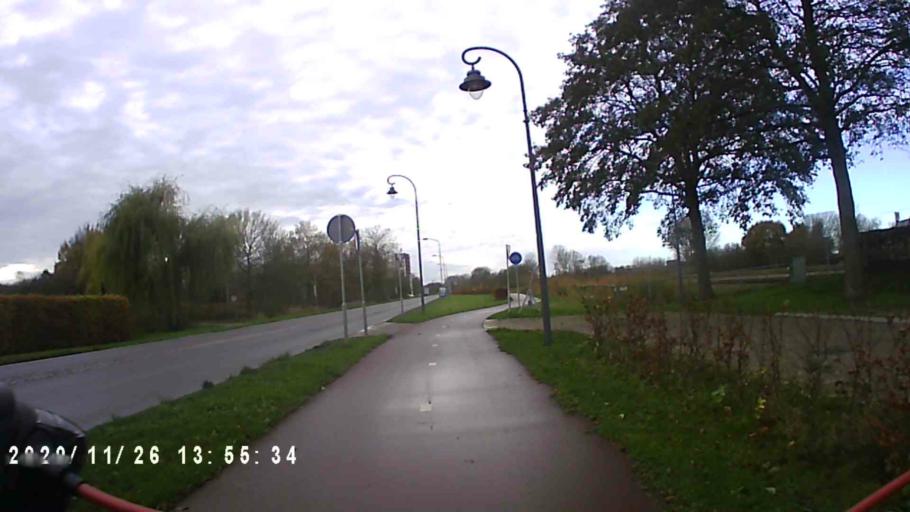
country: NL
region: Groningen
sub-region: Gemeente Delfzijl
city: Delfzijl
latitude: 53.3335
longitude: 6.9218
